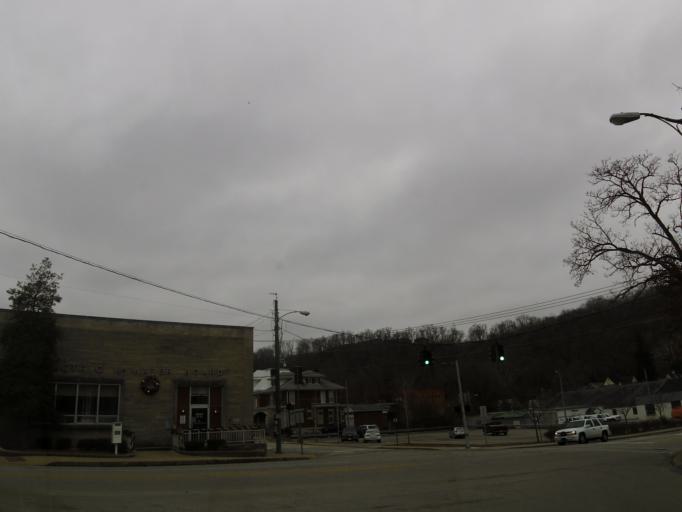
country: US
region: Kentucky
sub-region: Franklin County
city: Frankfort
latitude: 38.1952
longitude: -84.8790
